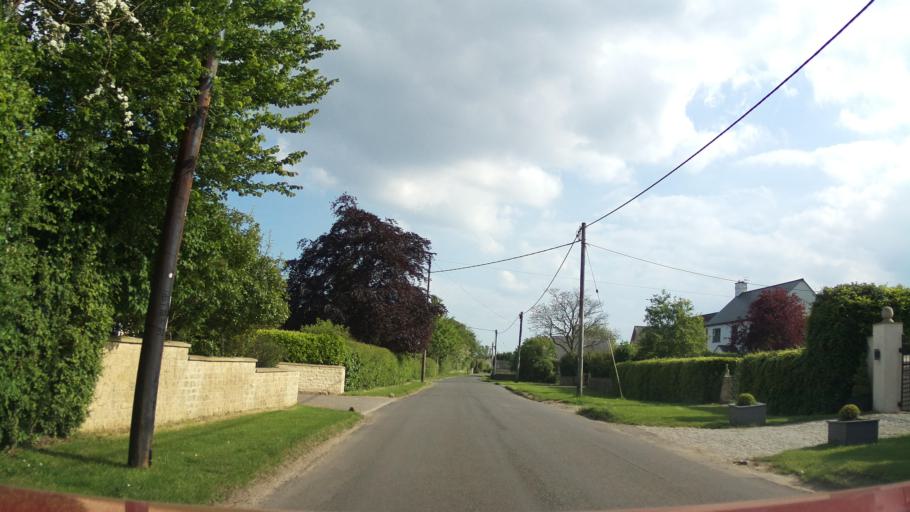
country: GB
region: England
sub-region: Wiltshire
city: Malmesbury
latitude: 51.5378
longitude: -2.0801
